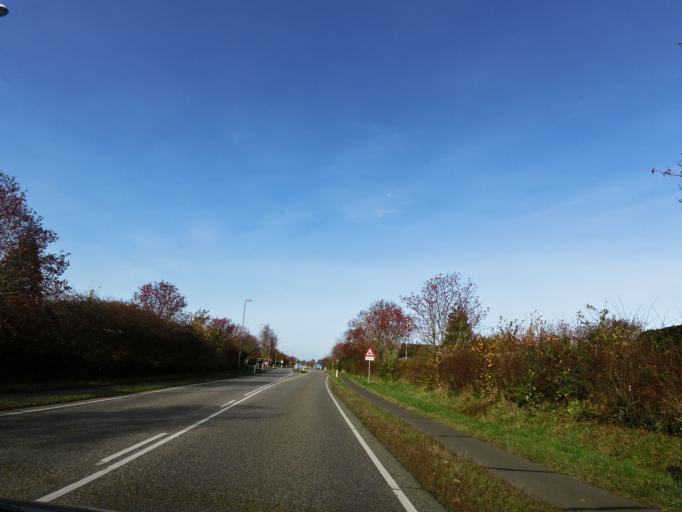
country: DK
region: Central Jutland
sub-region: Odder Kommune
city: Odder
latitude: 55.9182
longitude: 10.2501
